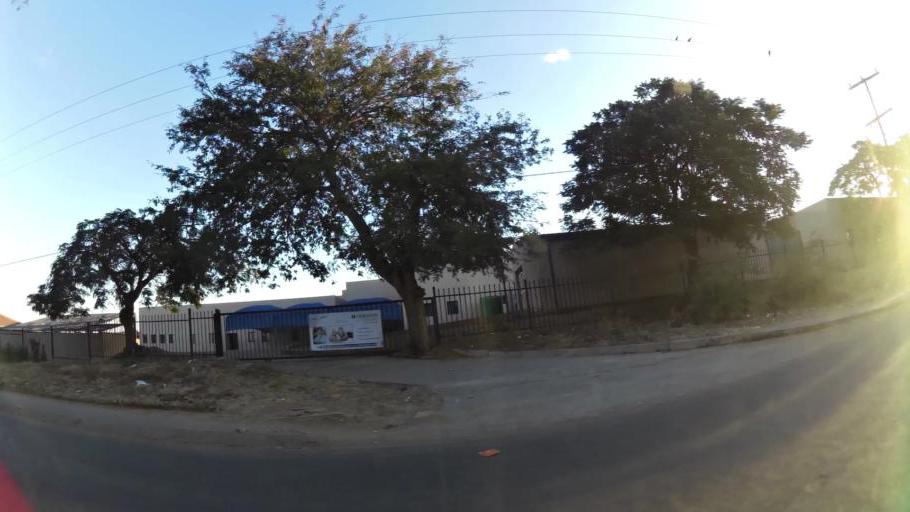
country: ZA
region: North-West
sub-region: Bojanala Platinum District Municipality
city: Rustenburg
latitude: -25.6446
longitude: 27.2129
